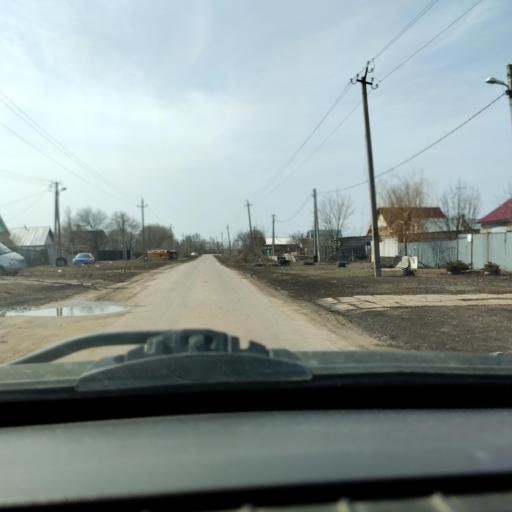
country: RU
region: Samara
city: Smyshlyayevka
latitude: 53.1786
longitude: 50.4420
